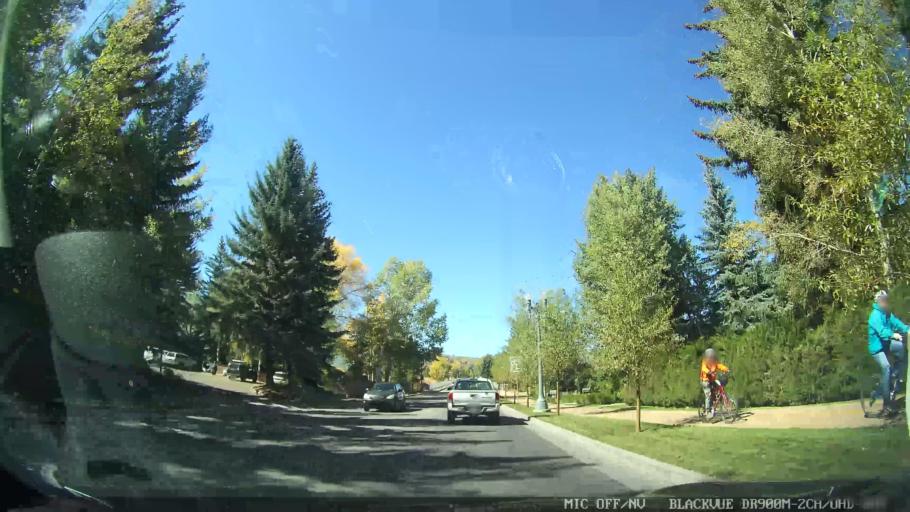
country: US
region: Colorado
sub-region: Pitkin County
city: Aspen
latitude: 39.1951
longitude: -106.8313
